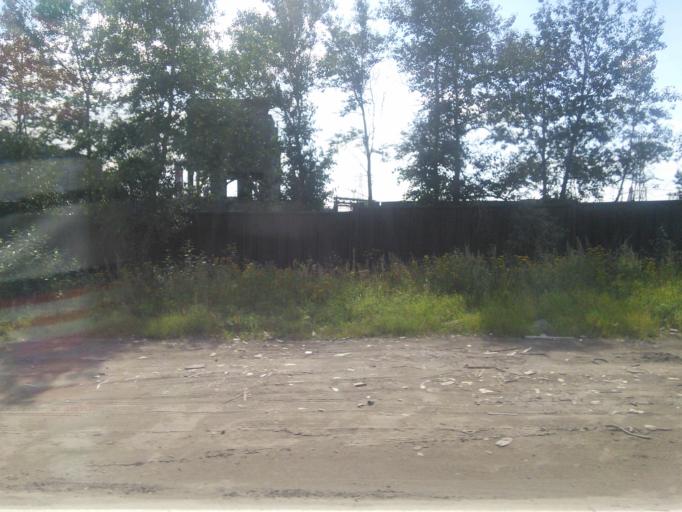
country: RU
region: Vologda
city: Cherepovets
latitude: 59.1537
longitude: 37.8663
